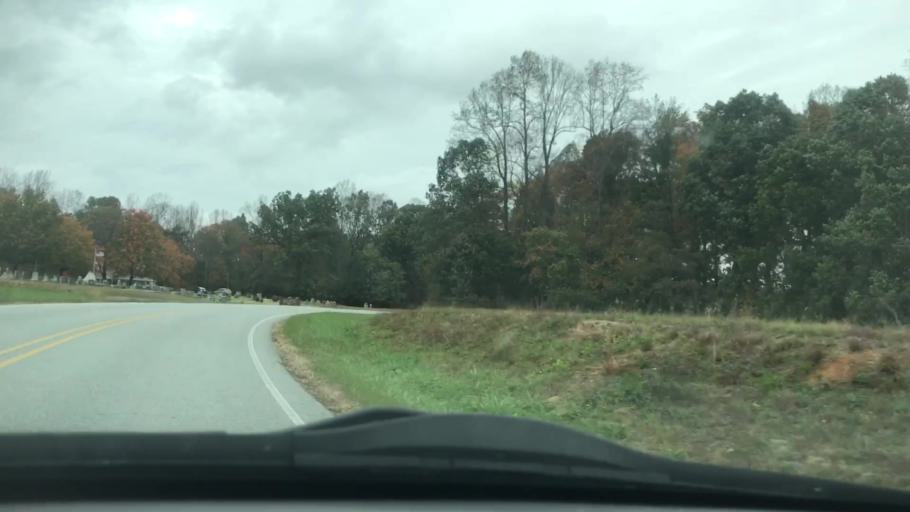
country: US
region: North Carolina
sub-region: Randolph County
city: Randleman
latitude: 35.7948
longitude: -79.8602
